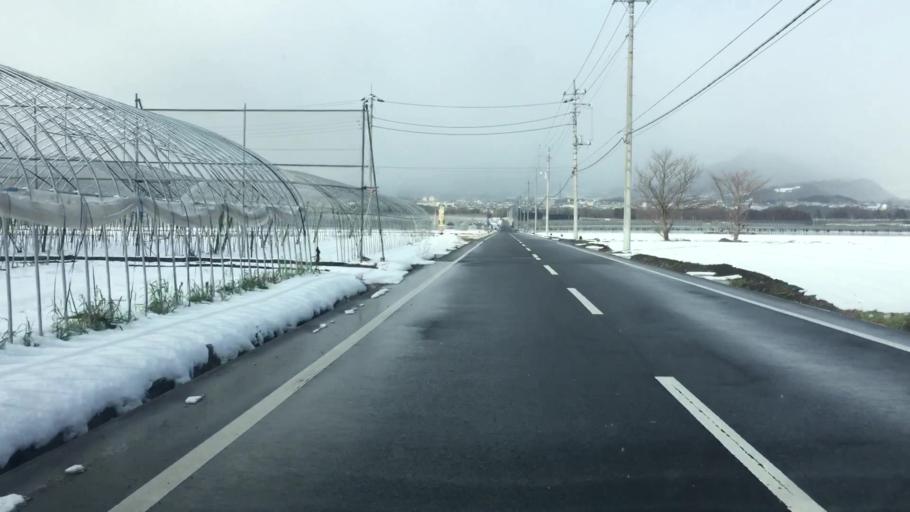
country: JP
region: Gunma
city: Numata
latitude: 36.6283
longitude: 139.0922
